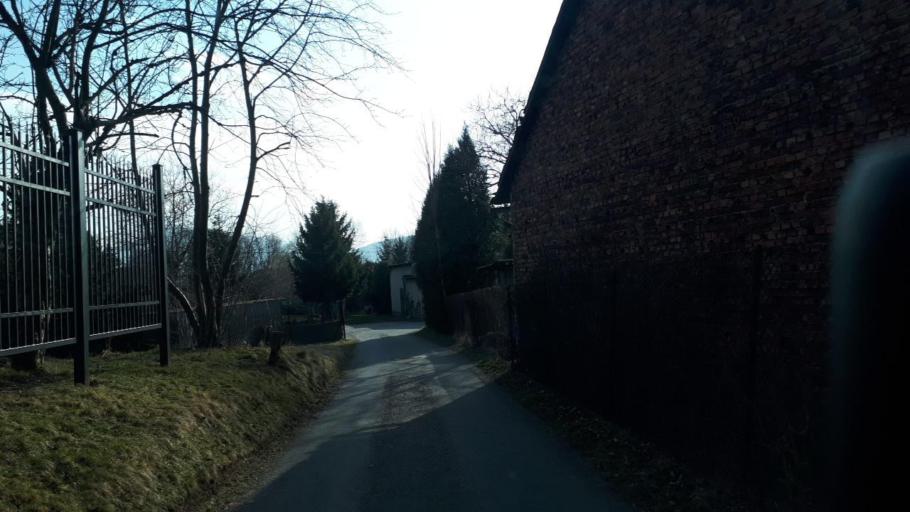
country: PL
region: Silesian Voivodeship
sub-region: Powiat bielski
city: Wilkowice
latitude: 49.7649
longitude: 19.0919
